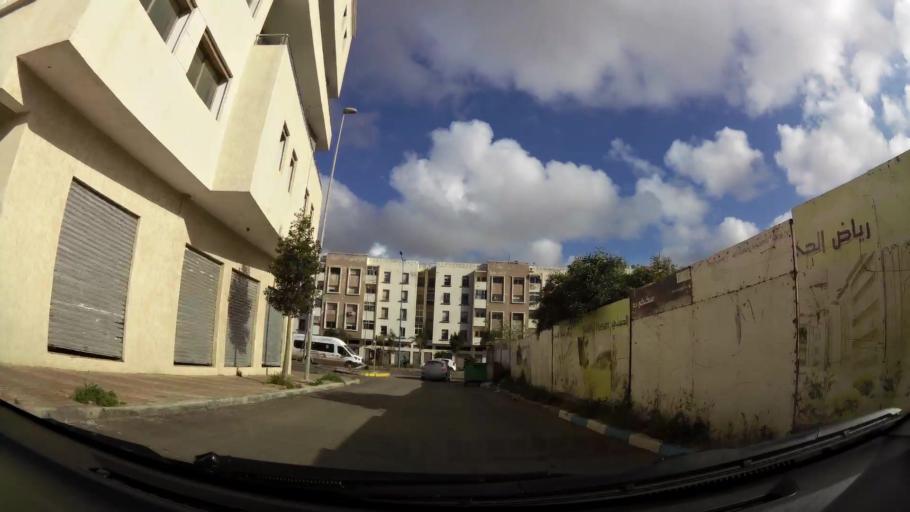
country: MA
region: Grand Casablanca
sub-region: Casablanca
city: Casablanca
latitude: 33.5493
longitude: -7.7005
